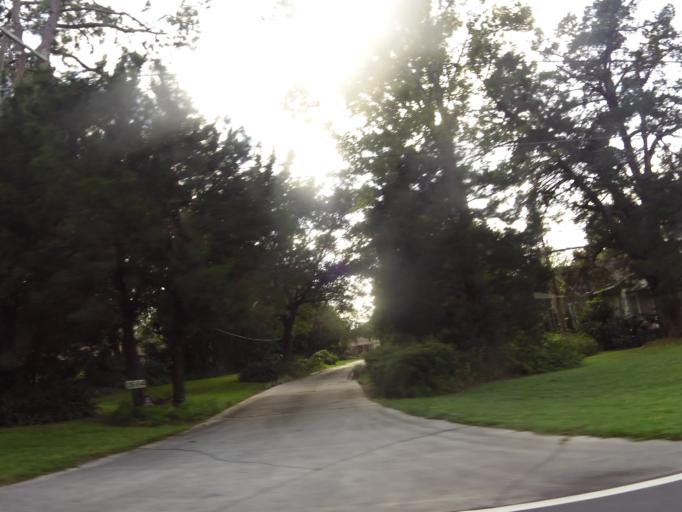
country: US
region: Florida
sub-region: Clay County
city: Bellair-Meadowbrook Terrace
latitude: 30.2713
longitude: -81.7288
